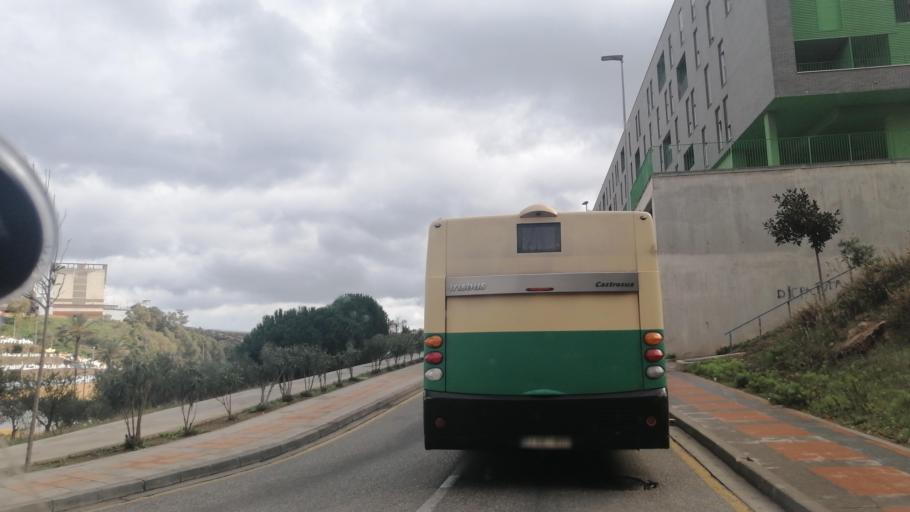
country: ES
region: Ceuta
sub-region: Ceuta
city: Ceuta
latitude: 35.8827
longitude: -5.3430
